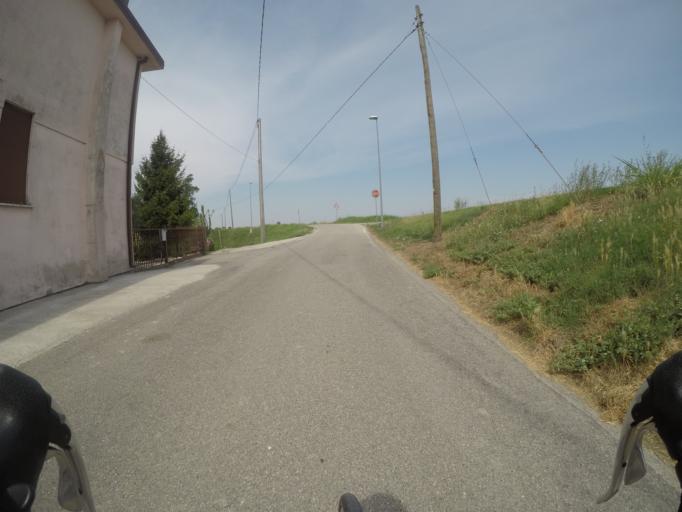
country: IT
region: Veneto
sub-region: Provincia di Rovigo
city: Villanova del Ghebbo Canton
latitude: 45.0494
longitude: 11.6577
